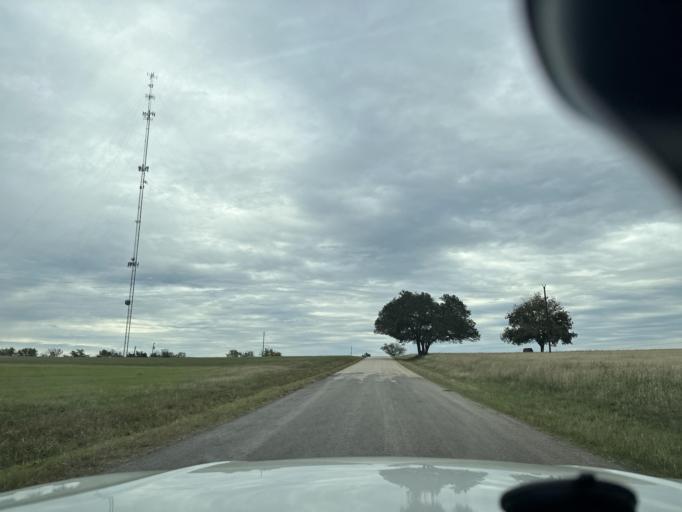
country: US
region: Texas
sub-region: Burleson County
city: Somerville
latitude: 30.1544
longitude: -96.6366
